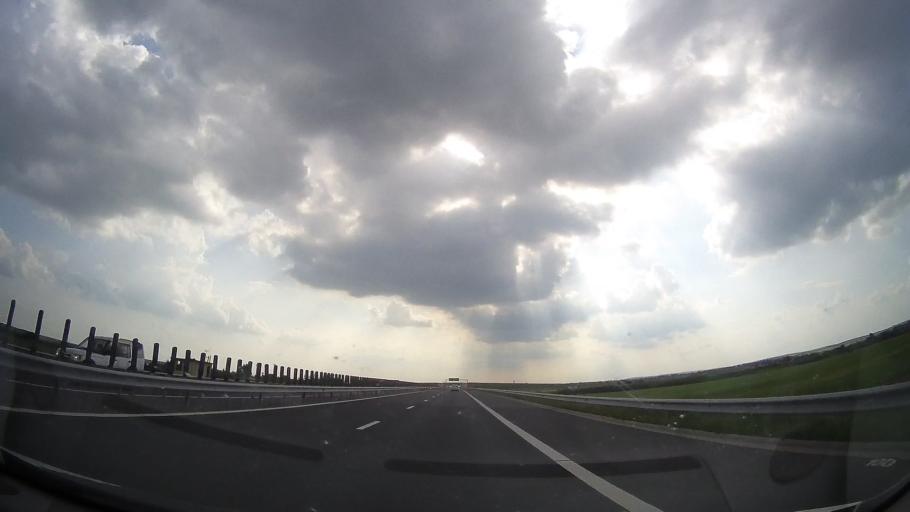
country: RO
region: Timis
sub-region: Comuna Balint
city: Balint
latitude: 45.8001
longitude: 21.8708
